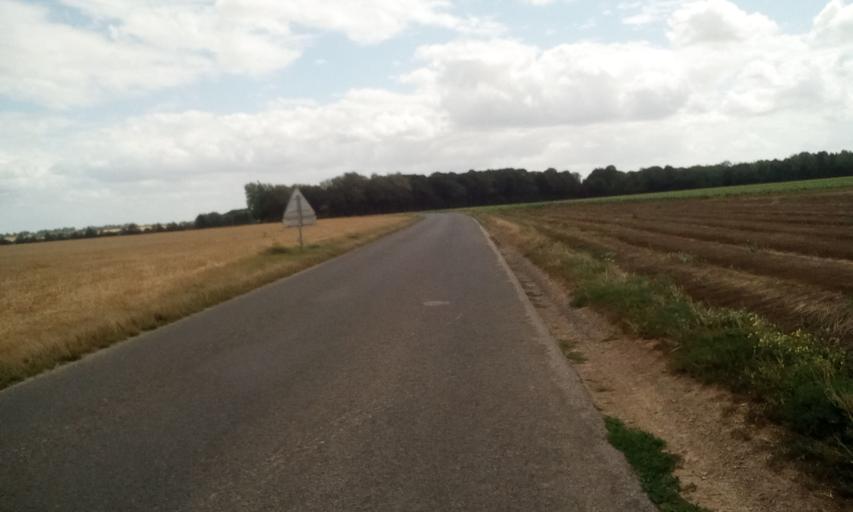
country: FR
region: Lower Normandy
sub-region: Departement du Calvados
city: Creully
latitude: 49.2749
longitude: -0.5308
